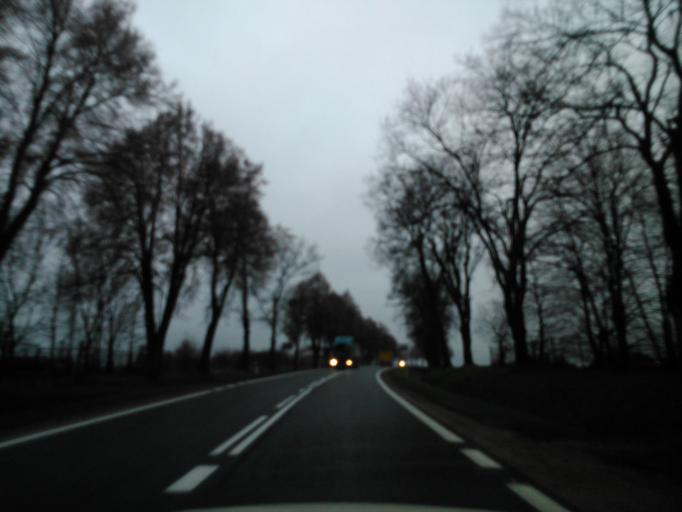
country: PL
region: Swietokrzyskie
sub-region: Powiat opatowski
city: Wojciechowice
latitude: 50.8344
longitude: 21.6281
